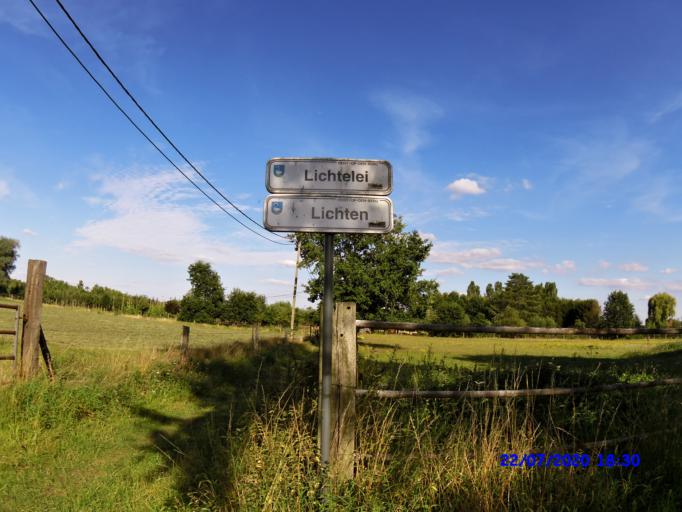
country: BE
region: Flanders
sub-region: Provincie Vlaams-Brabant
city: Begijnendijk
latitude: 51.0425
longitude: 4.7704
